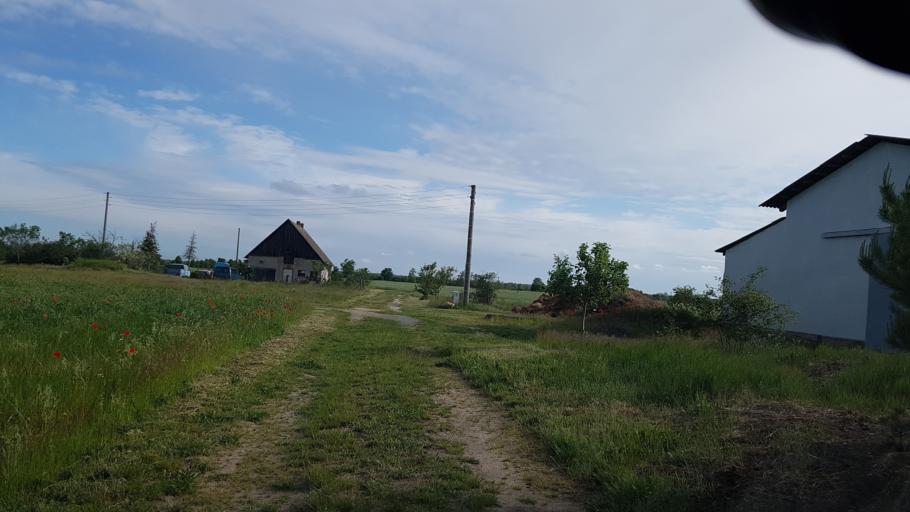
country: DE
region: Brandenburg
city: Crinitz
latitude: 51.8098
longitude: 13.8259
